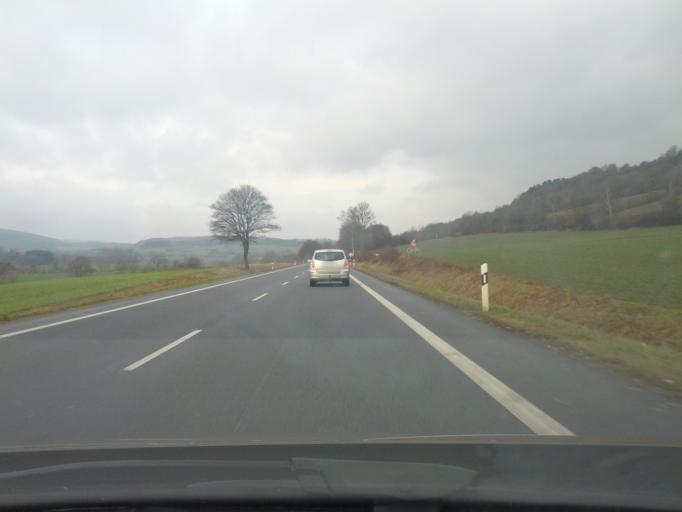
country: DE
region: Hesse
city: Witzenhausen
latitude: 51.3652
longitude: 9.8179
